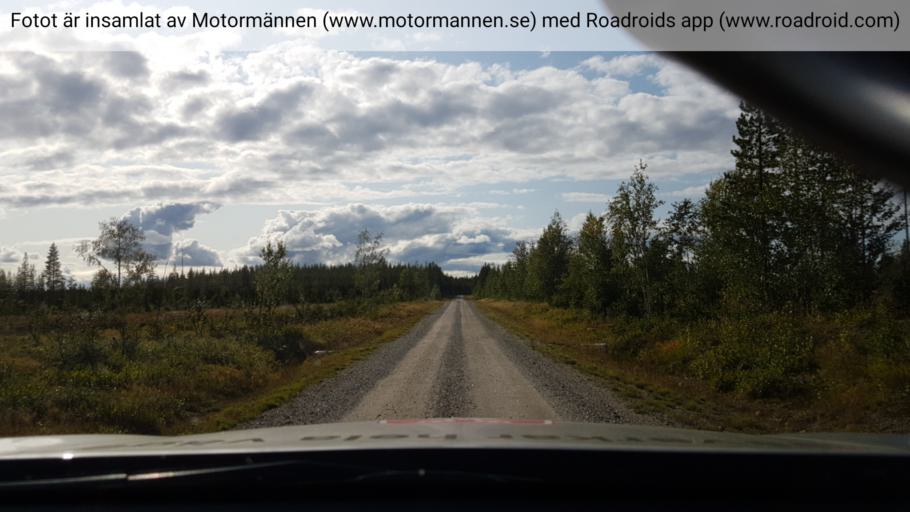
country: SE
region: Vaesterbotten
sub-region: Lycksele Kommun
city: Lycksele
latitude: 64.7164
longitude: 18.9731
